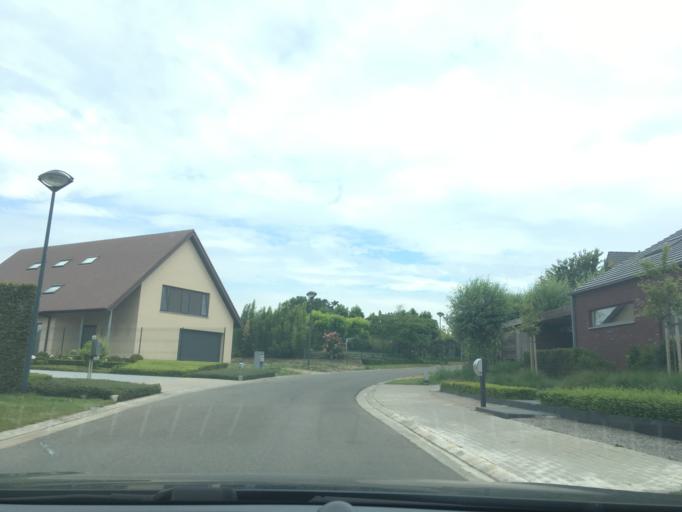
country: BE
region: Flanders
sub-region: Provincie West-Vlaanderen
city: Tielt
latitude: 50.9896
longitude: 3.3201
